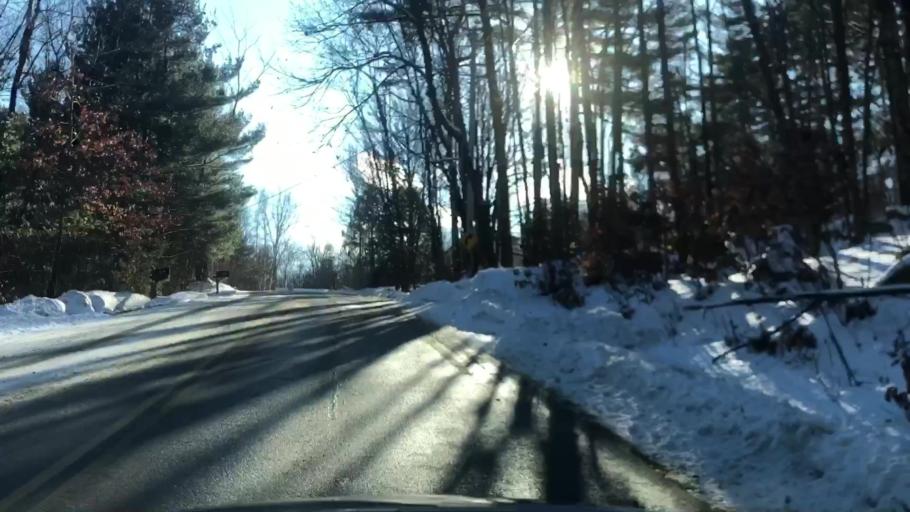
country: US
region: New Hampshire
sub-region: Hillsborough County
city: Wilton
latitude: 42.8183
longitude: -71.7215
